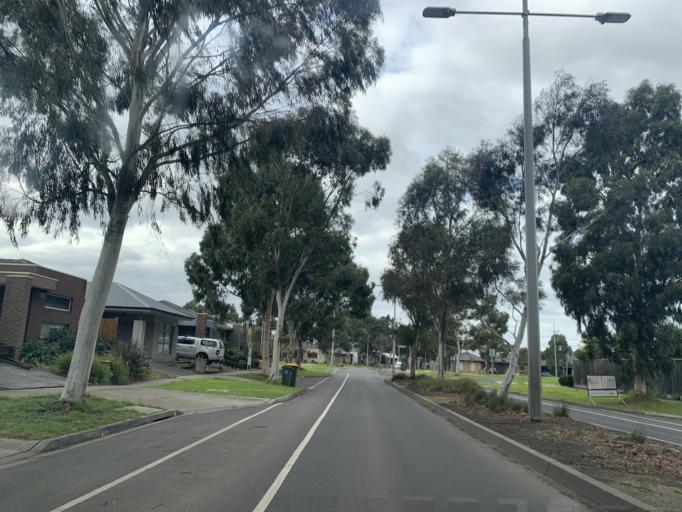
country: AU
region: Victoria
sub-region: Whittlesea
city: Epping
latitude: -37.6300
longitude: 145.0068
